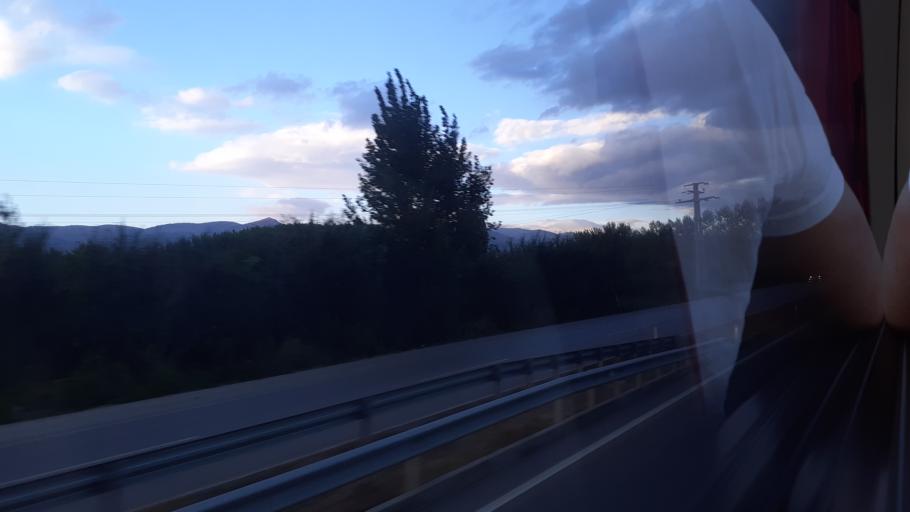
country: TR
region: Tokat
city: Dokmetepe
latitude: 40.3213
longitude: 36.1984
